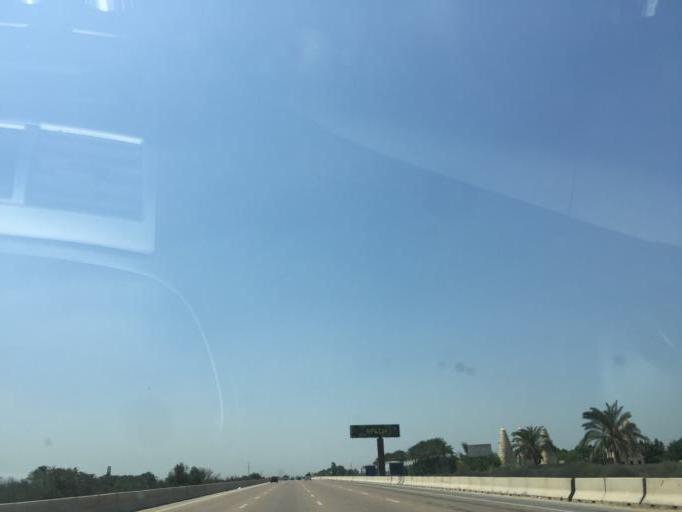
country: EG
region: Al Buhayrah
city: Abu al Matamir
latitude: 30.7642
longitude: 29.9820
